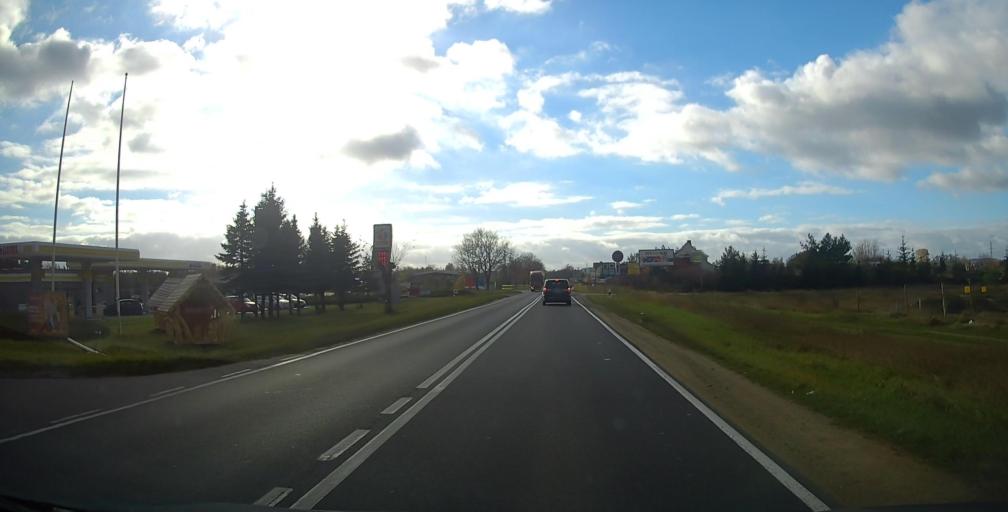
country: PL
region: Warmian-Masurian Voivodeship
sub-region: Powiat elcki
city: Elk
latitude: 53.7752
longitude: 22.3434
